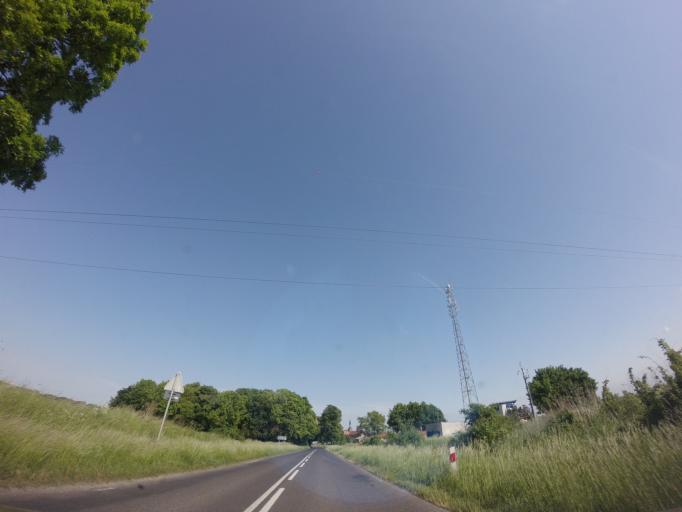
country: PL
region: West Pomeranian Voivodeship
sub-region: Powiat gryfinski
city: Stare Czarnowo
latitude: 53.3035
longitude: 14.8055
